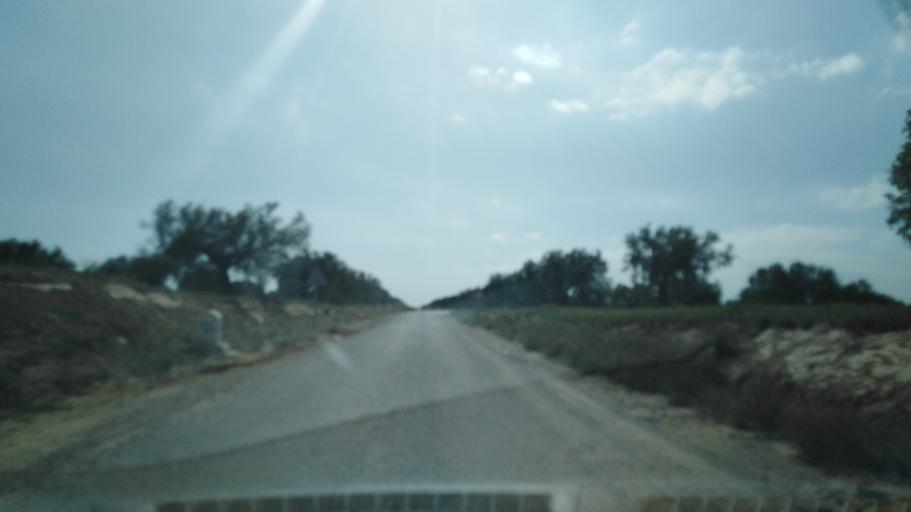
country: TN
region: Safaqis
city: Bi'r `Ali Bin Khalifah
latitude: 34.7767
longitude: 10.3645
